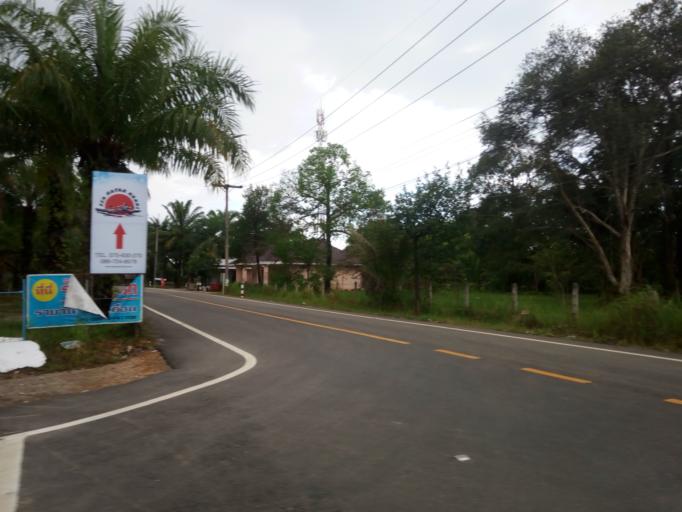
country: TH
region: Phangnga
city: Ban Ao Nang
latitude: 8.1448
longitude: 98.7442
